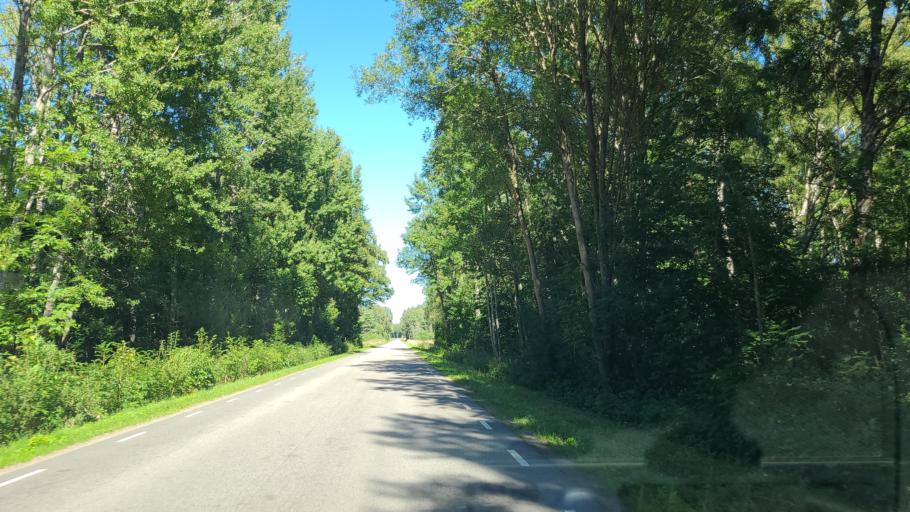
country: SE
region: Kalmar
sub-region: Borgholms Kommun
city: Borgholm
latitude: 56.8234
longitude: 16.7591
